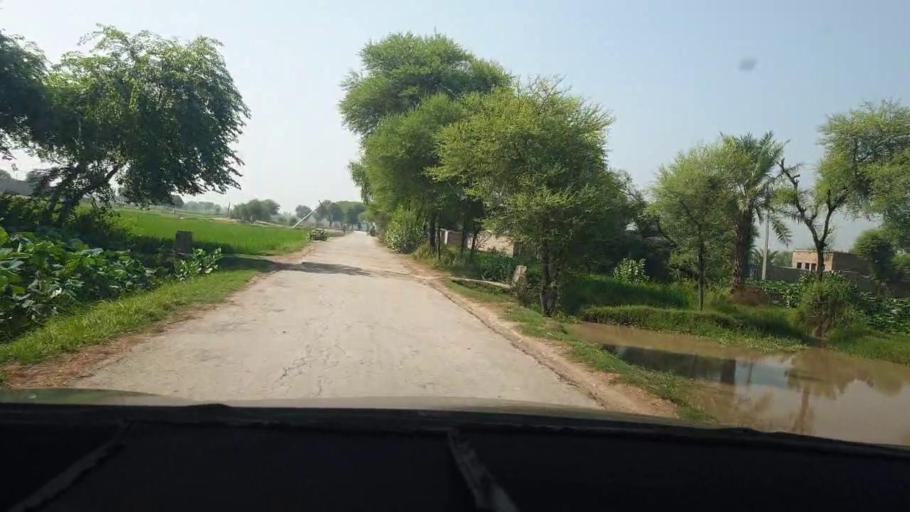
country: PK
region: Sindh
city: Kambar
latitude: 27.5713
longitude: 68.0562
